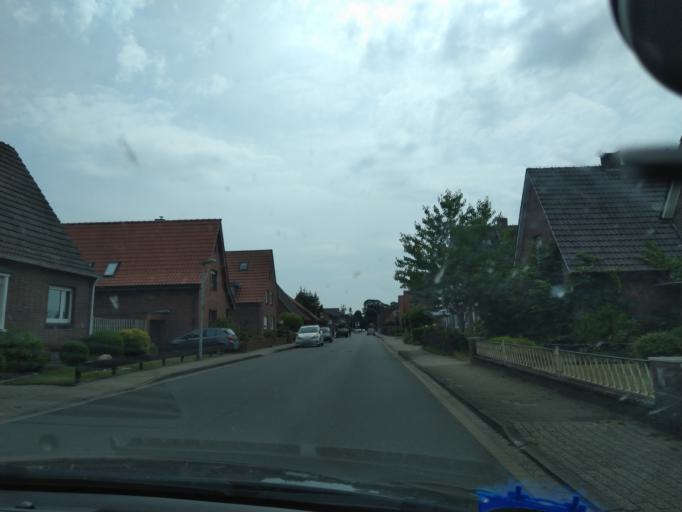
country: DE
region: Lower Saxony
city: Nordhorn
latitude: 52.4551
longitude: 7.0610
